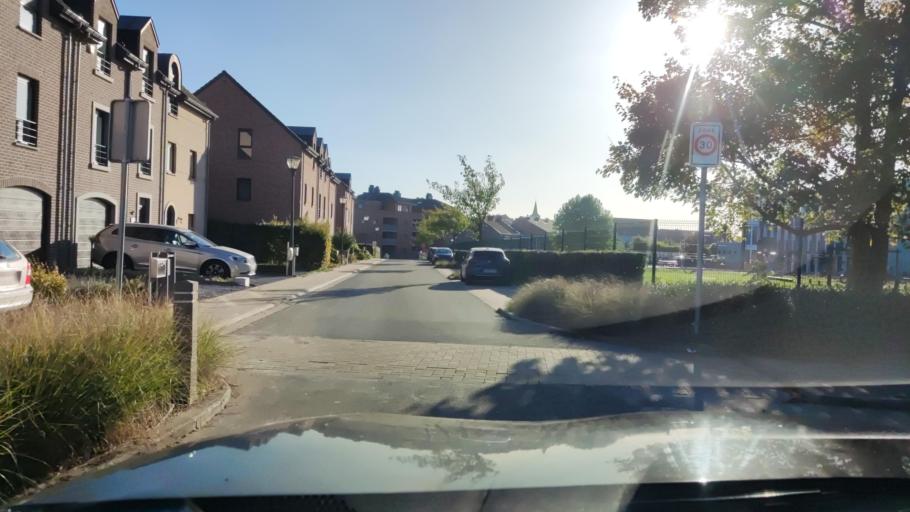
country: BE
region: Wallonia
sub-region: Province du Brabant Wallon
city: Jodoigne
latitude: 50.7256
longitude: 4.8753
